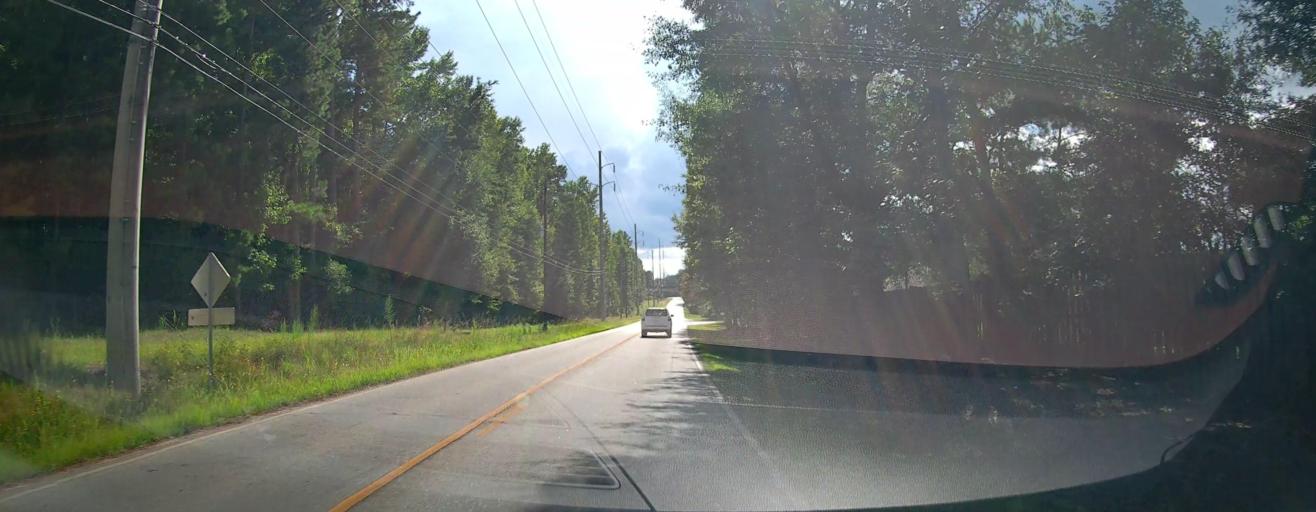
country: US
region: Georgia
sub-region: Muscogee County
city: Columbus
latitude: 32.5529
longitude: -84.8717
